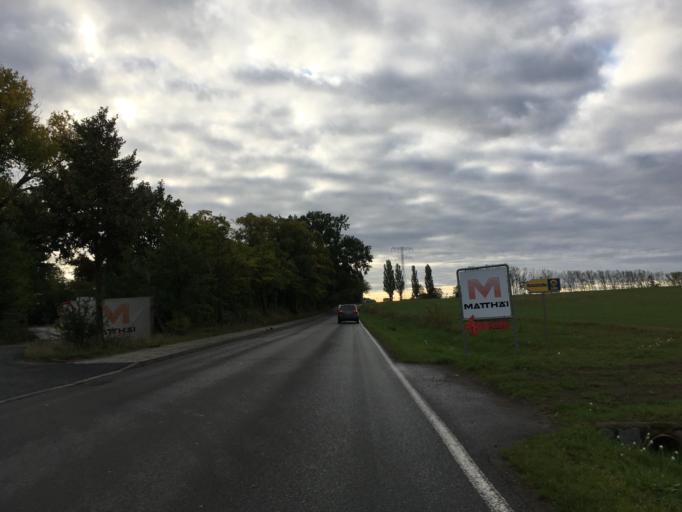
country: DE
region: Berlin
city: Wartenberg
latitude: 52.5951
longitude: 13.5246
